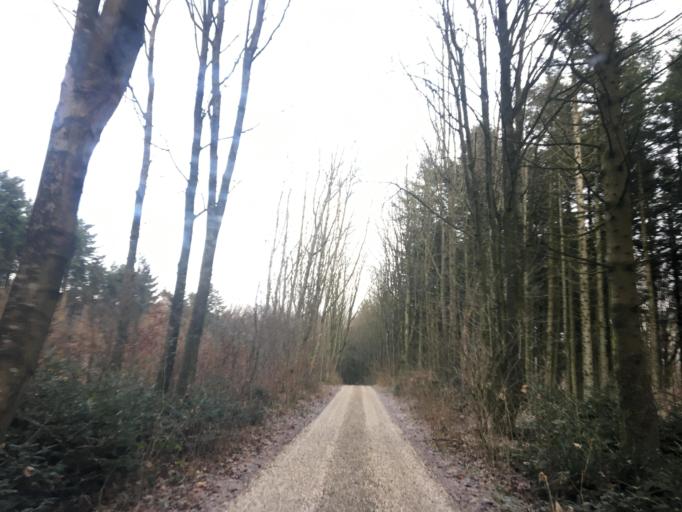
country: DK
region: North Denmark
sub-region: Thisted Kommune
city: Hurup
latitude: 56.7546
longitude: 8.3902
